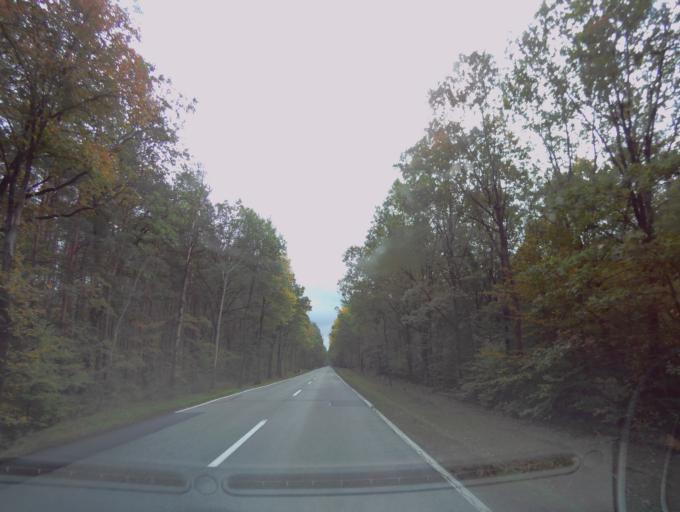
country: PL
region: Subcarpathian Voivodeship
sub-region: Powiat nizanski
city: Krzeszow
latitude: 50.3965
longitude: 22.2979
